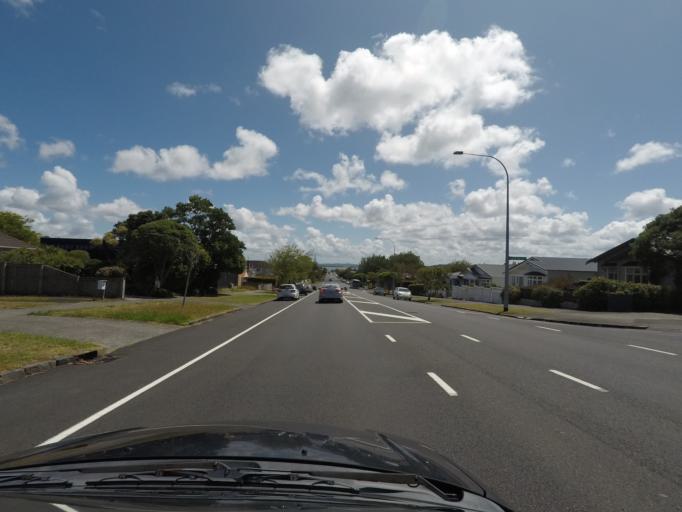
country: NZ
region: Auckland
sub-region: Auckland
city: Auckland
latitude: -36.8577
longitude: 174.7223
